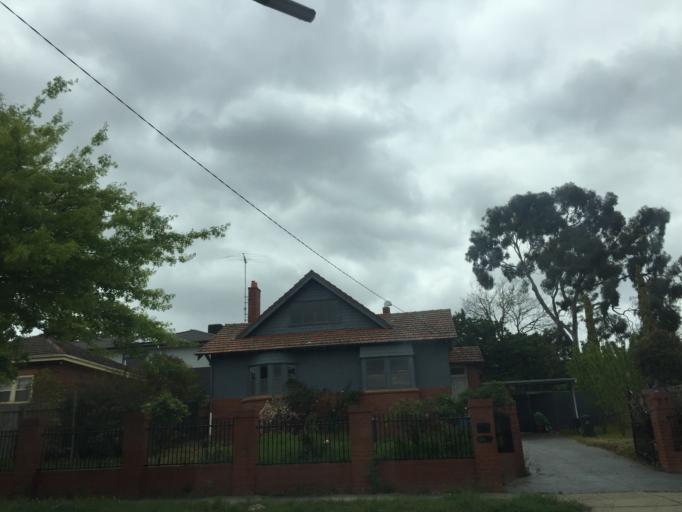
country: AU
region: Victoria
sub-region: Boroondara
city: Kew East
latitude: -37.8074
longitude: 145.0538
